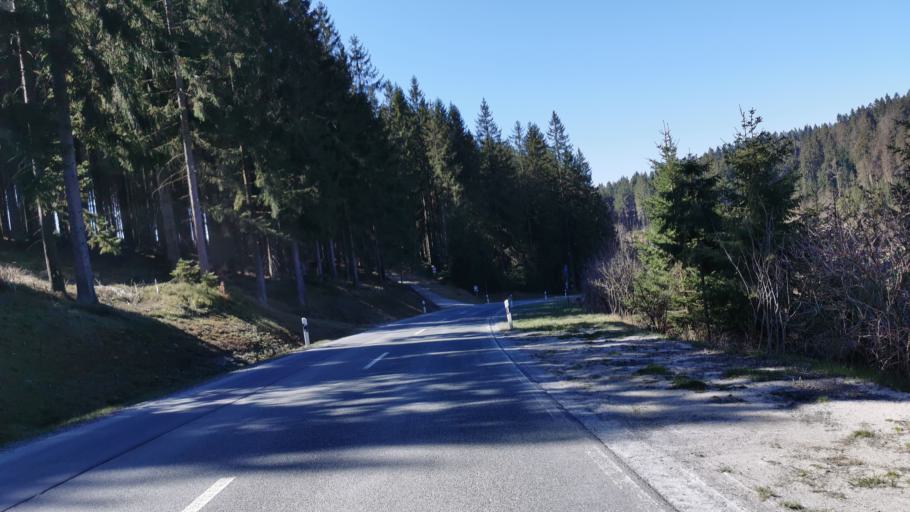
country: DE
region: Bavaria
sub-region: Upper Franconia
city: Ludwigsstadt
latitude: 50.4470
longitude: 11.3456
